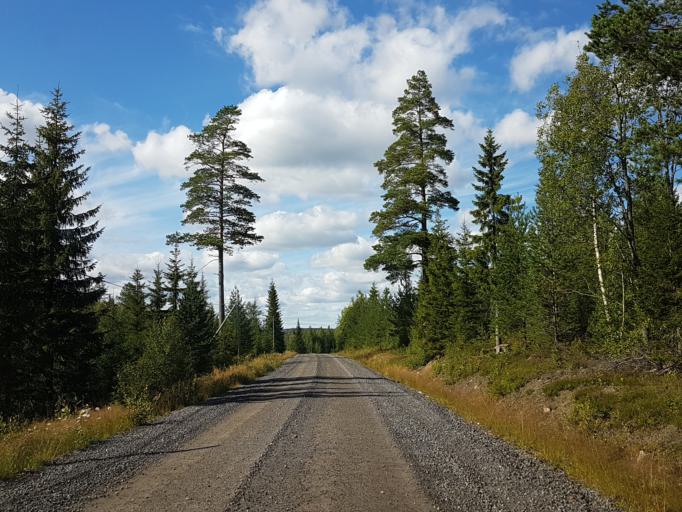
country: SE
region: Vaesterbotten
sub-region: Skelleftea Kommun
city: Burtraesk
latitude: 64.2840
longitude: 20.4631
